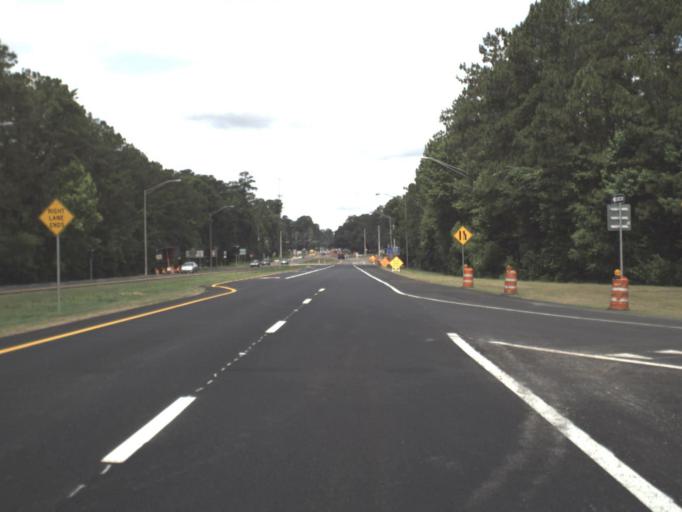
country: US
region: Florida
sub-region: Nassau County
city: Nassau Village-Ratliff
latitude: 30.4384
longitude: -81.7268
